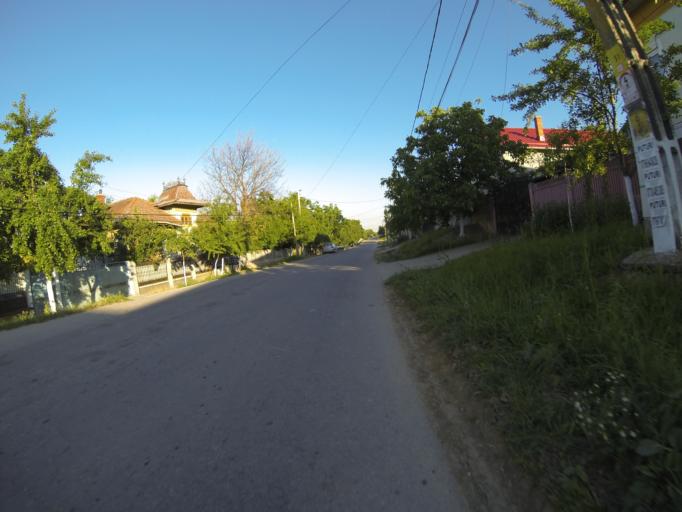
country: RO
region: Dolj
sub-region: Comuna Tuglui
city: Tuglui
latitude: 44.1974
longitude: 23.8032
